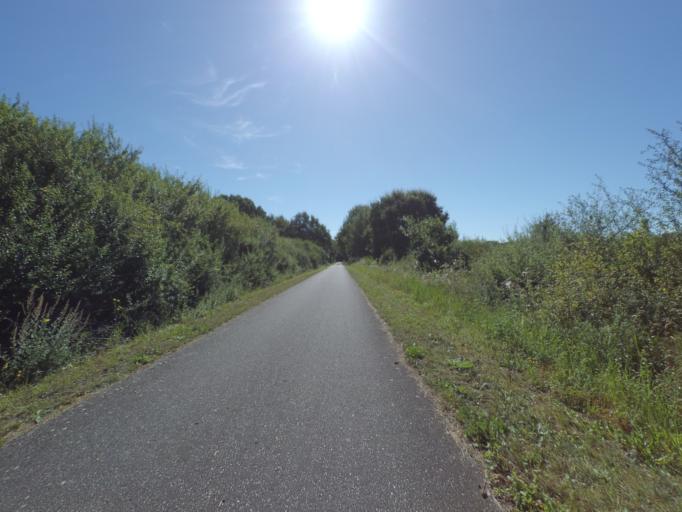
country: DE
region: Rheinland-Pfalz
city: Niederofflingen
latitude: 50.0699
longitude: 6.8902
